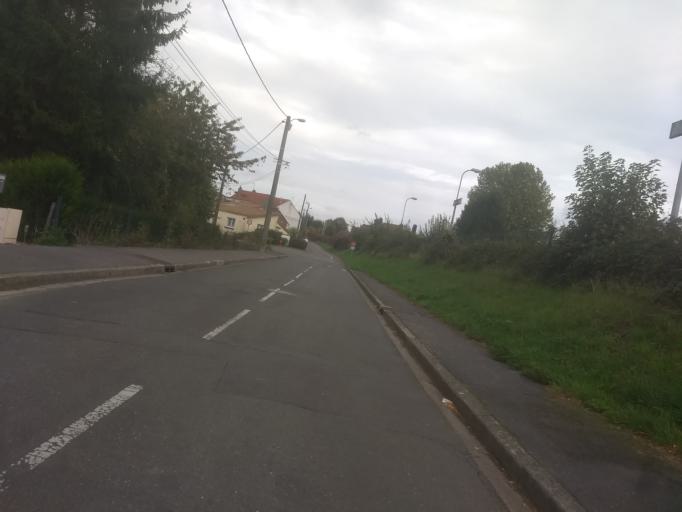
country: FR
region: Nord-Pas-de-Calais
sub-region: Departement du Pas-de-Calais
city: Achicourt
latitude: 50.2782
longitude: 2.7611
